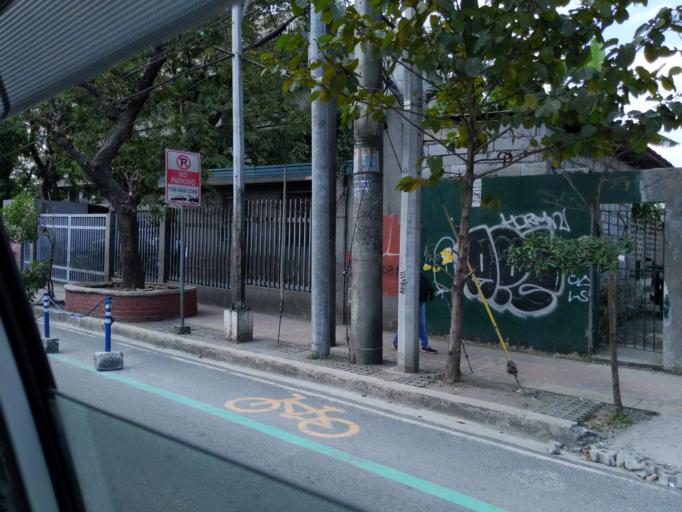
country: PH
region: Metro Manila
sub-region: Quezon City
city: Quezon City
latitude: 14.6384
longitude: 121.0462
